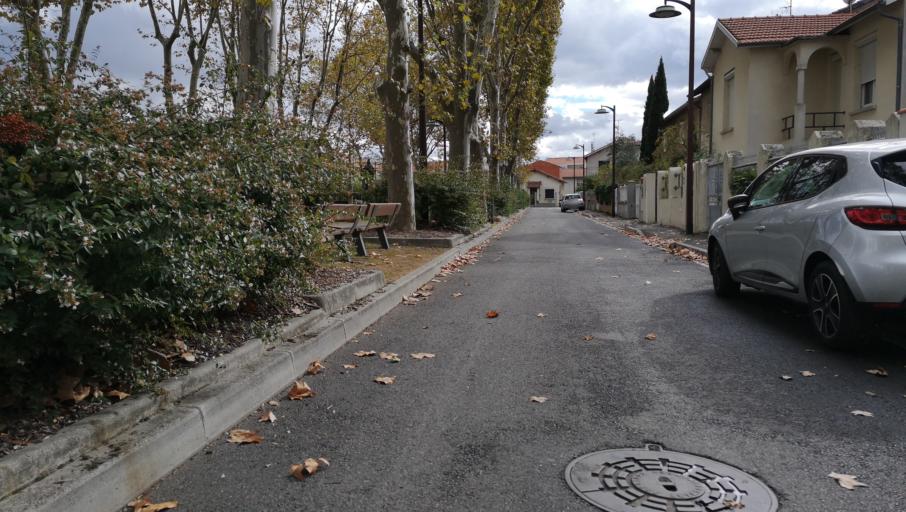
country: FR
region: Midi-Pyrenees
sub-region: Departement de la Haute-Garonne
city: Toulouse
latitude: 43.6054
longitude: 1.4118
